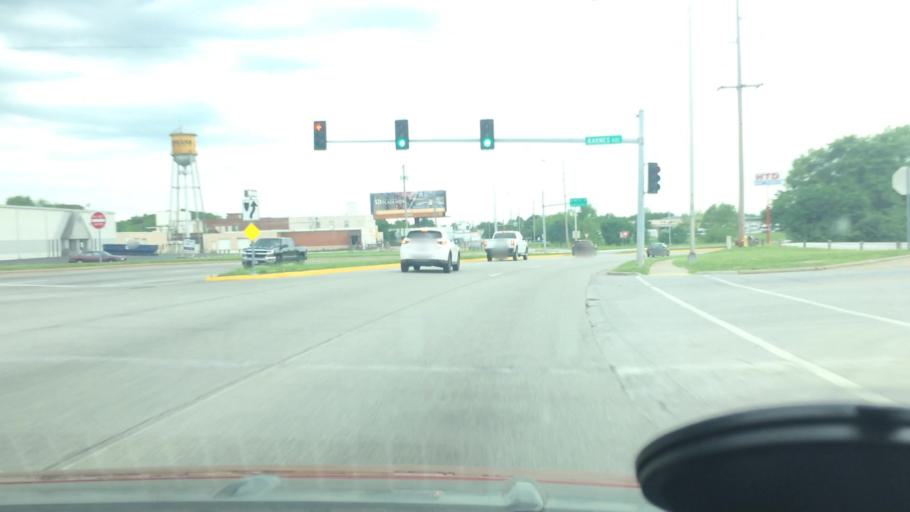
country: US
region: Missouri
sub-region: Greene County
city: Springfield
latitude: 37.2105
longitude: -93.2524
